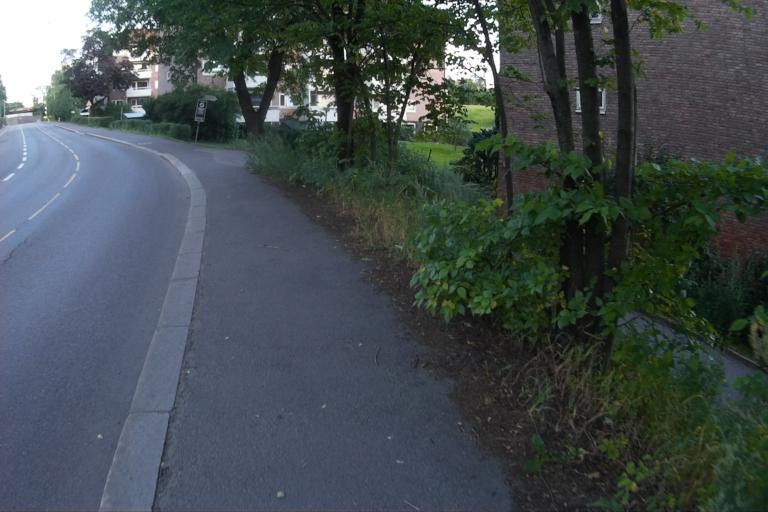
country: NO
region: Oslo
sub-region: Oslo
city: Oslo
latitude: 59.9251
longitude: 10.7789
